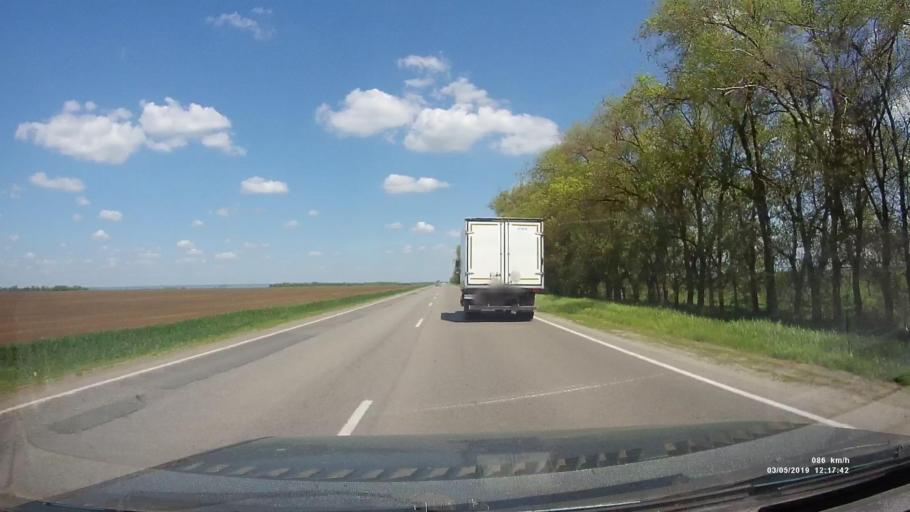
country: RU
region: Rostov
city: Melikhovskaya
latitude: 47.3853
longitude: 40.5943
